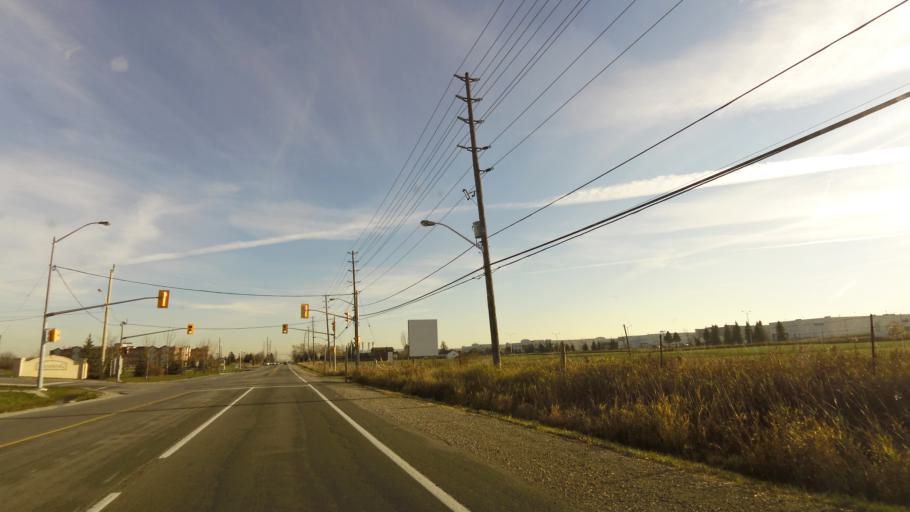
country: CA
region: Ontario
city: Brampton
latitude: 43.7591
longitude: -79.6926
